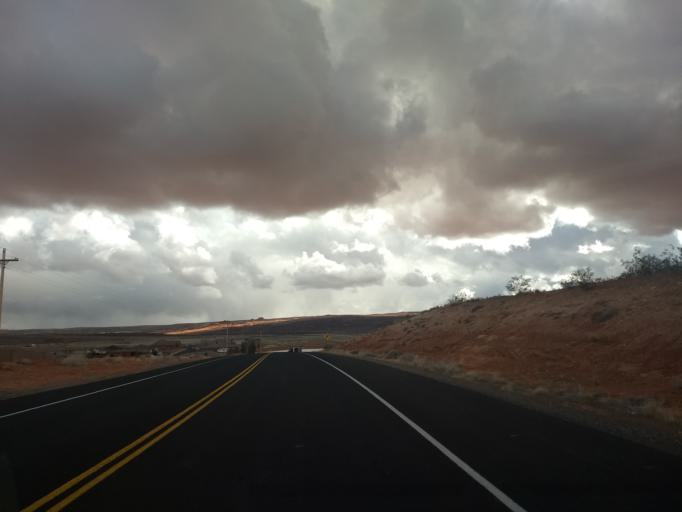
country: US
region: Utah
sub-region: Washington County
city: Hurricane
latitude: 37.1394
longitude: -113.3901
